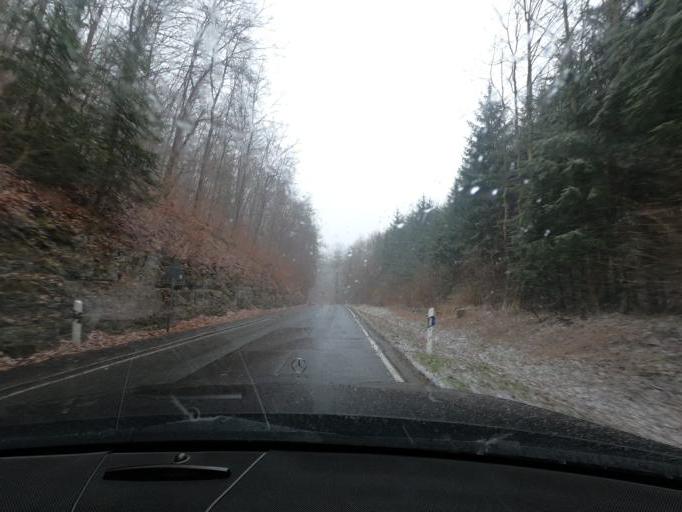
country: DE
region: Thuringia
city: Effelder
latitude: 51.2516
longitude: 10.2420
